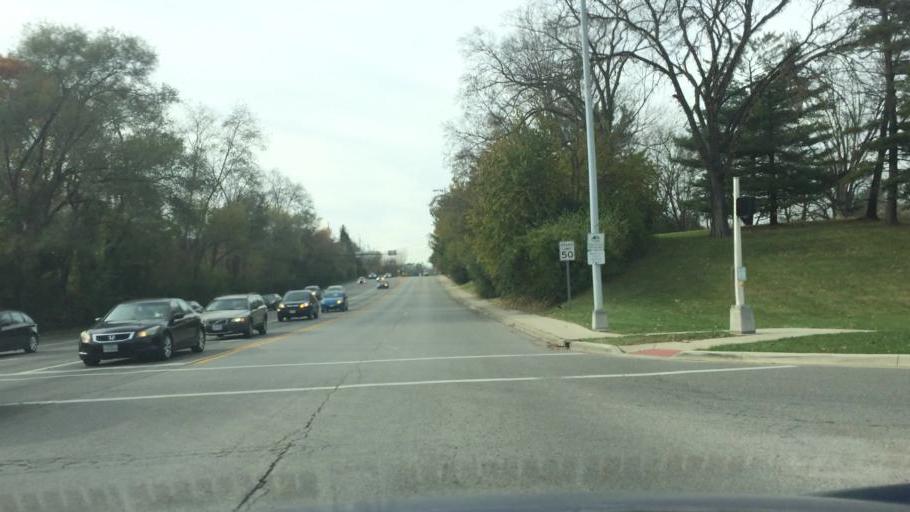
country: US
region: Ohio
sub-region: Franklin County
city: Worthington
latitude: 40.0520
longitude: -83.0339
